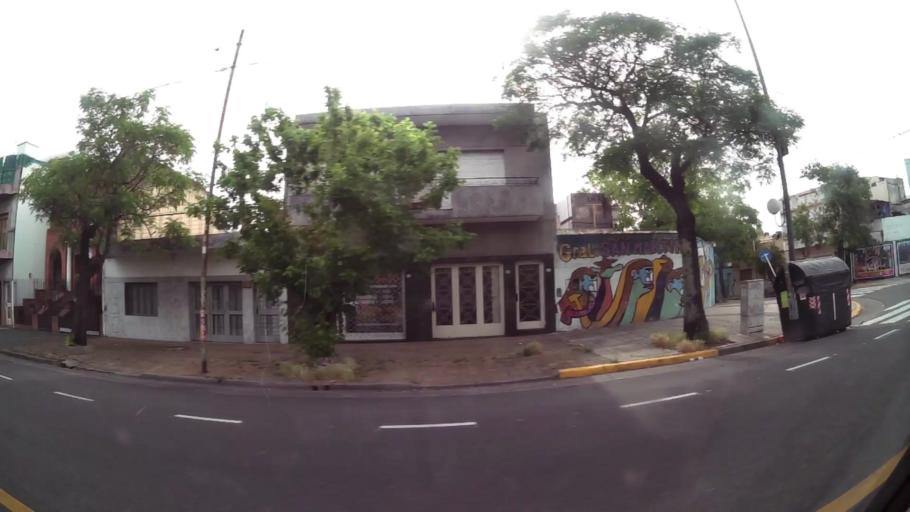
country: AR
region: Buenos Aires F.D.
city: Villa Lugano
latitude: -34.6429
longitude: -58.4309
